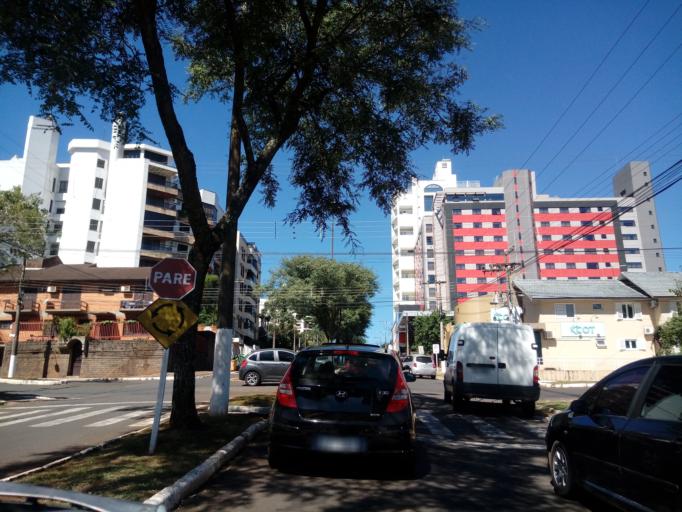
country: BR
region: Santa Catarina
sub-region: Chapeco
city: Chapeco
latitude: -27.1092
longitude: -52.6152
